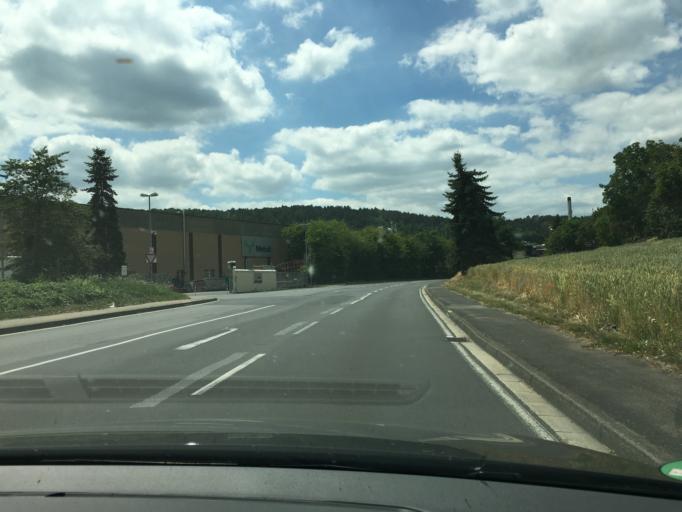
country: DE
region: North Rhine-Westphalia
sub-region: Regierungsbezirk Koln
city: Kreuzau
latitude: 50.7275
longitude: 6.4761
